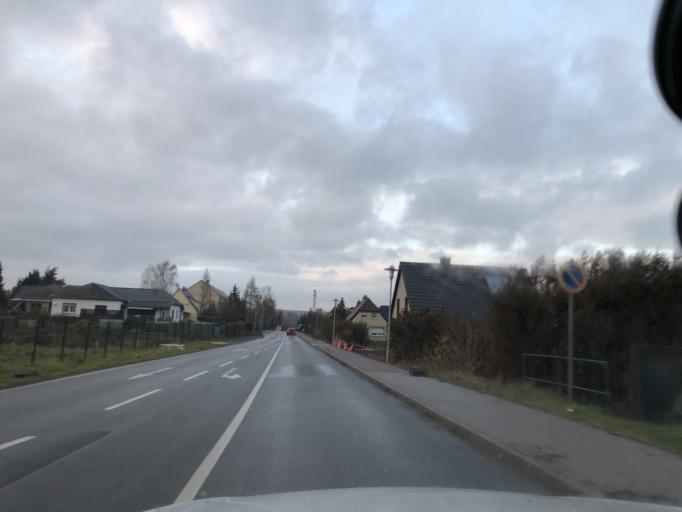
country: DE
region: Saxony-Anhalt
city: Langenbogen
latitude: 51.4803
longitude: 11.7797
